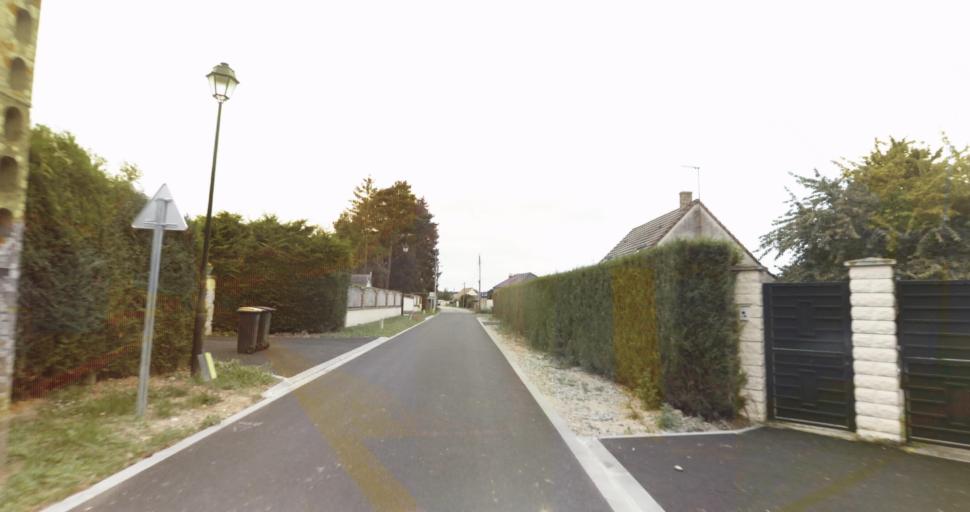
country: FR
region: Haute-Normandie
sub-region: Departement de l'Eure
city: Marcilly-sur-Eure
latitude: 48.8878
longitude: 1.3008
